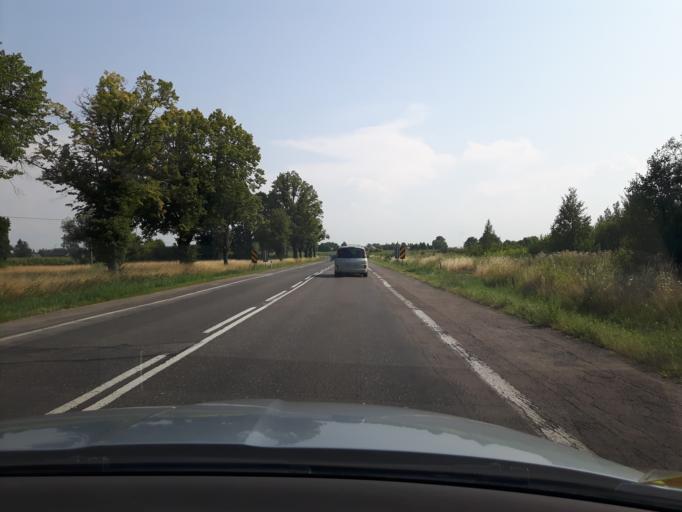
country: PL
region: Masovian Voivodeship
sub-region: Powiat plonski
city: Plonsk
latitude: 52.6640
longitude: 20.3747
